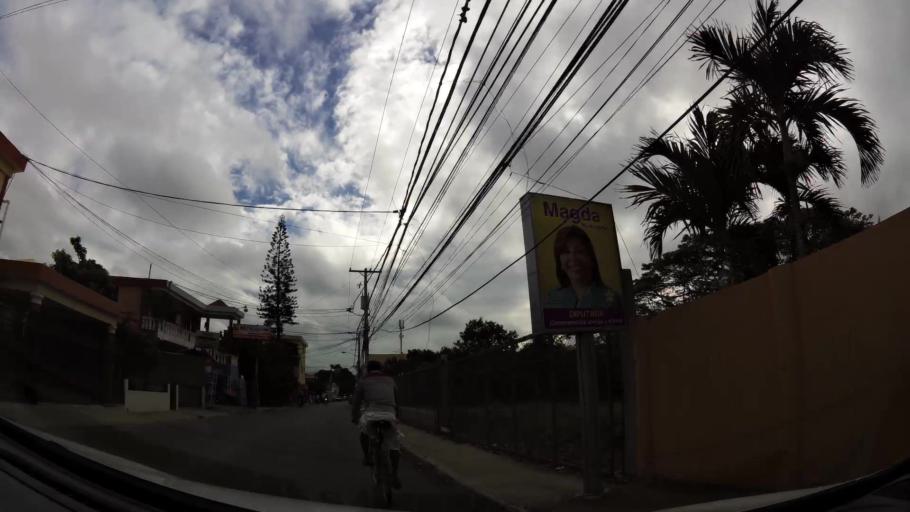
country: DO
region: Santiago
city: Santiago de los Caballeros
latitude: 19.4610
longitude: -70.6580
